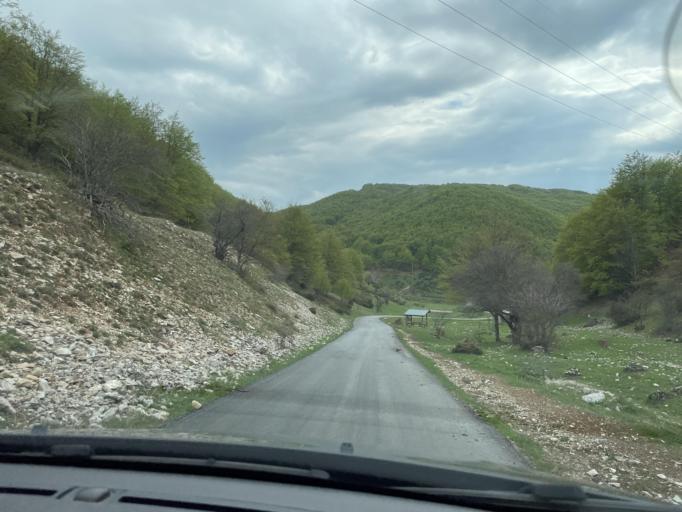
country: MK
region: Opstina Rostusa
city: Rostusha
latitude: 41.5975
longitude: 20.6747
